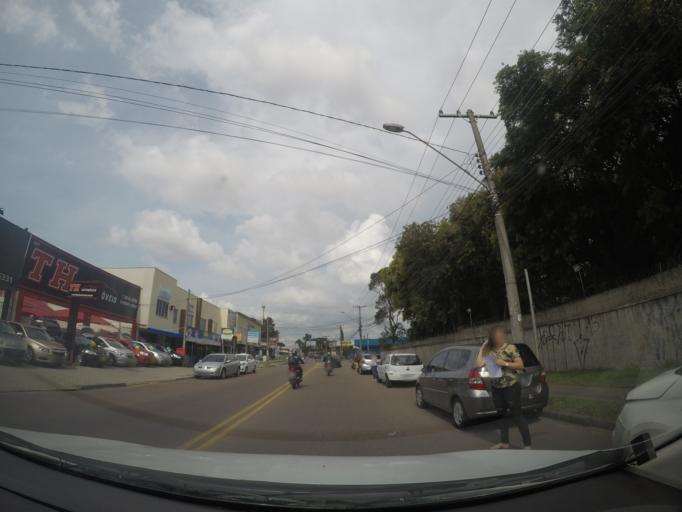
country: BR
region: Parana
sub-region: Sao Jose Dos Pinhais
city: Sao Jose dos Pinhais
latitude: -25.5002
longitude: -49.2669
